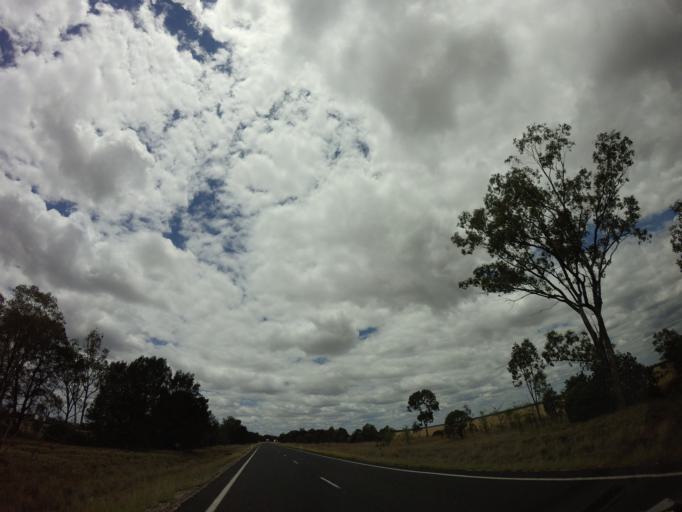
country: AU
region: Queensland
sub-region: Goondiwindi
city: Goondiwindi
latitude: -28.1652
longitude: 150.5332
